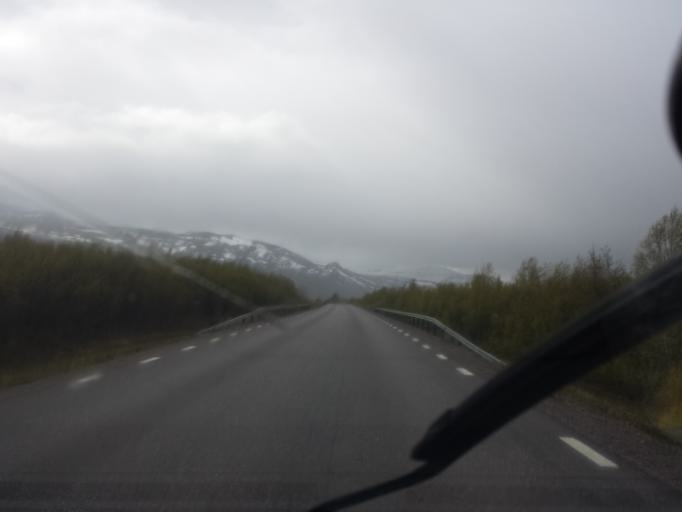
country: SE
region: Norrbotten
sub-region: Kiruna Kommun
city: Kiruna
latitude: 68.2327
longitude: 19.6096
